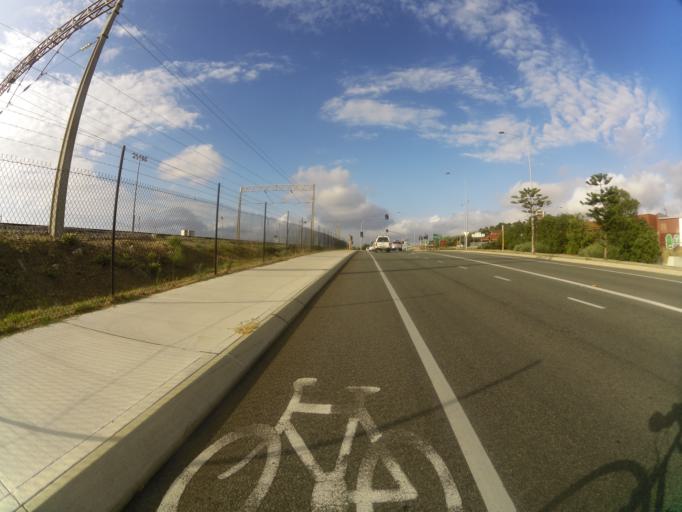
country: AU
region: Western Australia
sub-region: Fremantle
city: North Fremantle
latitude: -32.0445
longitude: 115.7525
